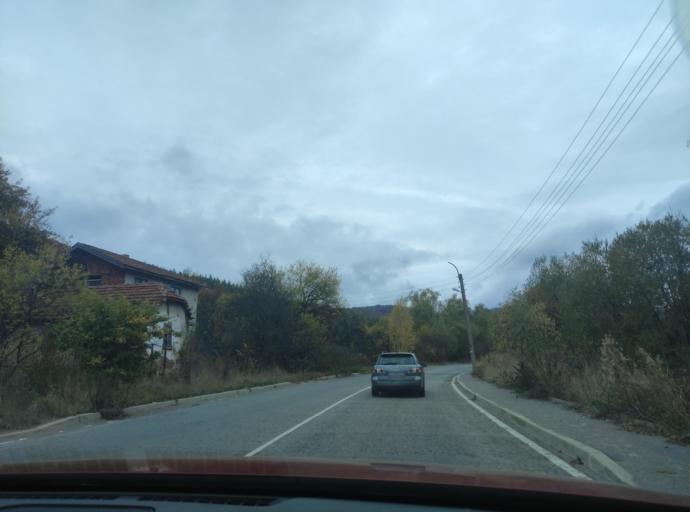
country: BG
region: Sofiya
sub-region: Obshtina Godech
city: Godech
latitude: 43.0904
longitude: 23.0981
